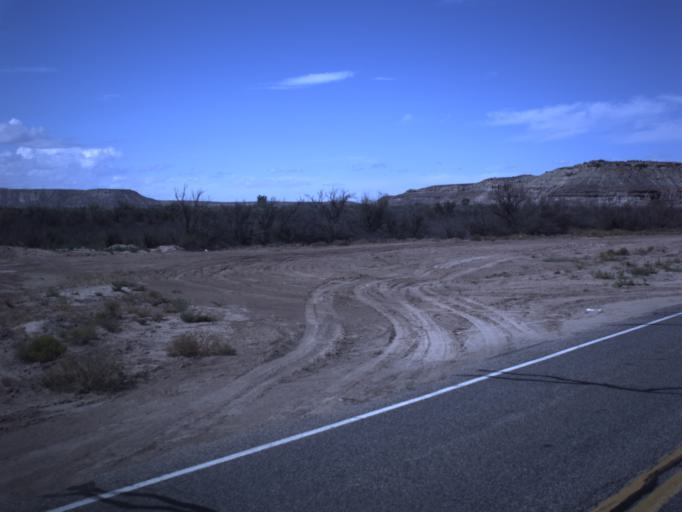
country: US
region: Utah
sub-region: San Juan County
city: Blanding
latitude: 37.2542
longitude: -109.2592
